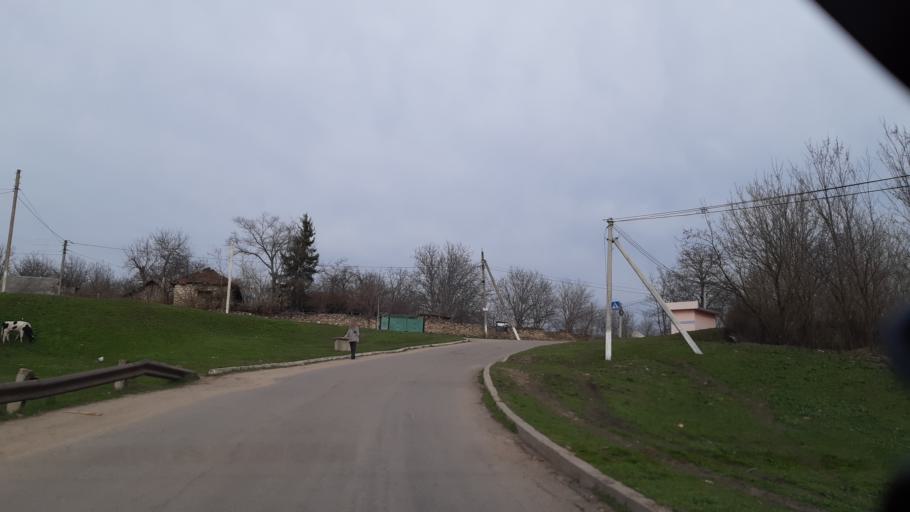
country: MD
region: Soldanesti
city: Soldanesti
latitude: 47.6854
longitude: 28.7774
